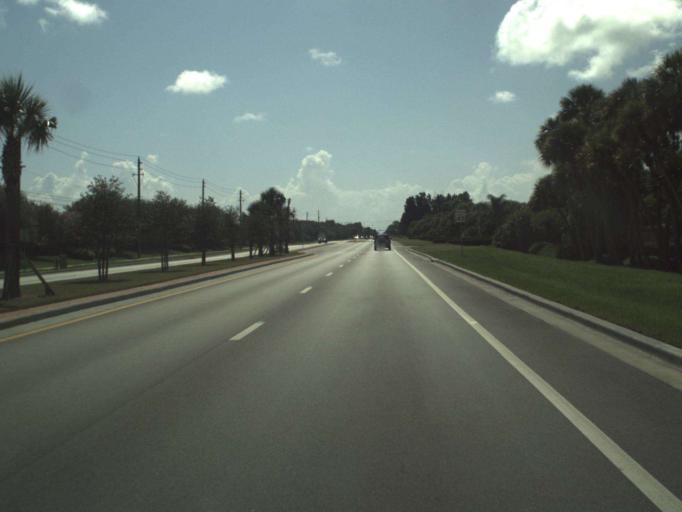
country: US
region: Florida
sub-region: Indian River County
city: Vero Beach South
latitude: 27.5874
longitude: -80.4397
